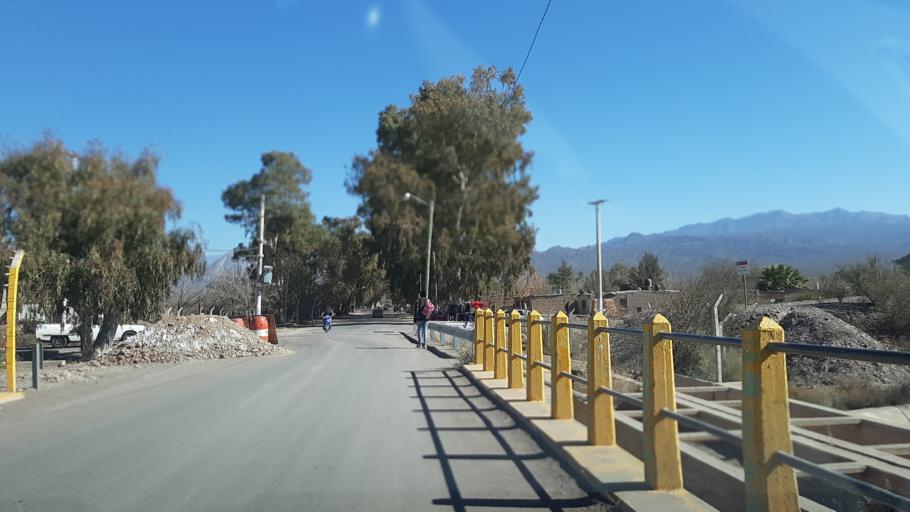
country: AR
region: San Juan
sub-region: Departamento de Zonda
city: Zonda
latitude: -31.4693
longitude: -68.7343
